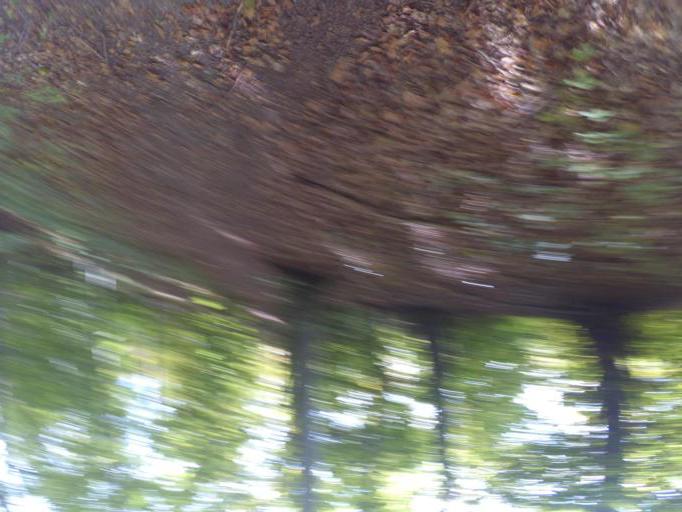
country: DE
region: Baden-Wuerttemberg
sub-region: Regierungsbezirk Stuttgart
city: Heubach
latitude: 48.7803
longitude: 9.9178
